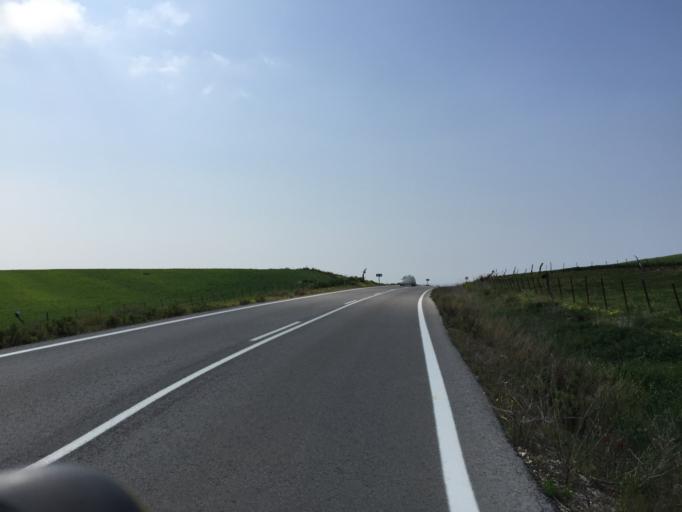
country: ES
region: Andalusia
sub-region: Provincia de Cadiz
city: Vejer de la Frontera
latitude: 36.2322
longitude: -6.0322
